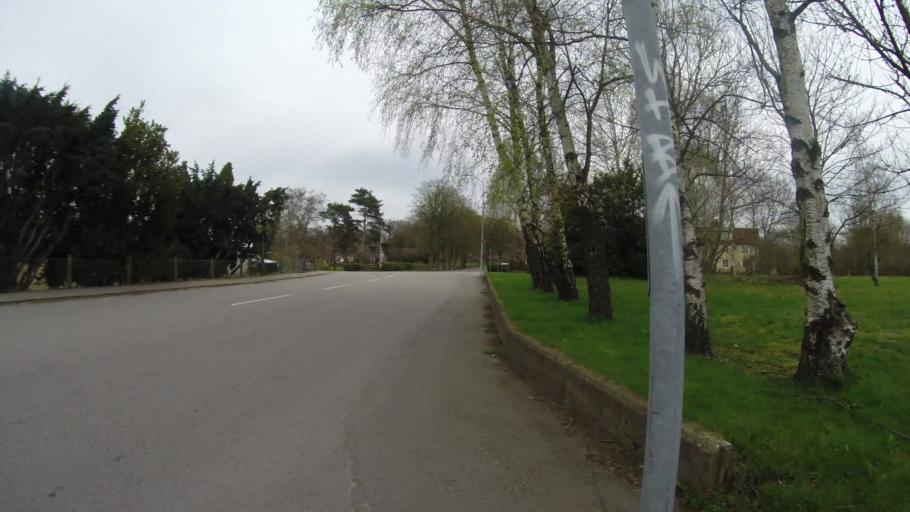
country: SE
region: Skane
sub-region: Bjuvs Kommun
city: Billesholm
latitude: 56.0511
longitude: 12.9759
